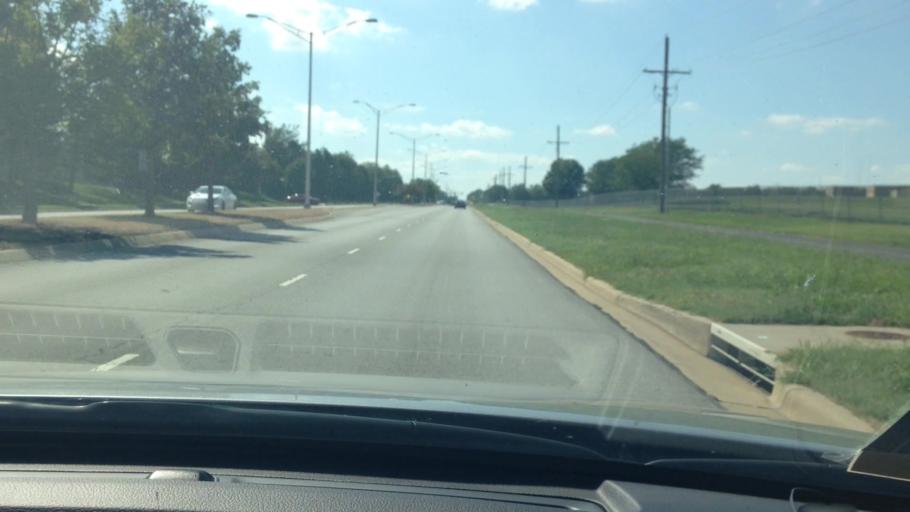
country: US
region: Kansas
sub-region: Johnson County
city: Lenexa
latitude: 38.8692
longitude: -94.6951
